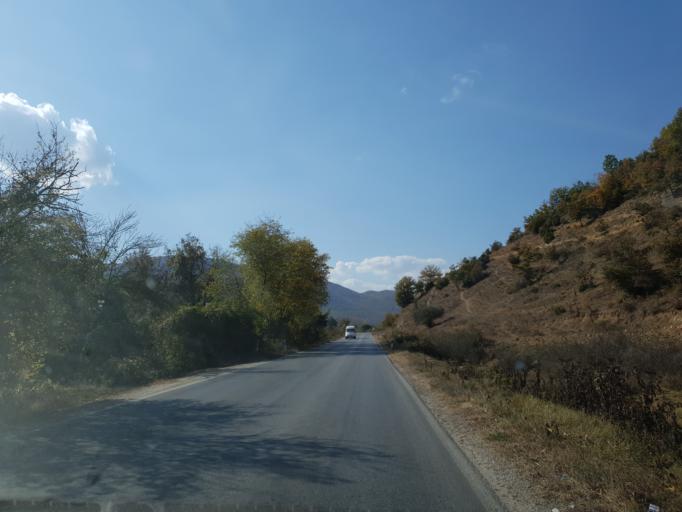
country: MK
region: Vranestica
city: Vranestica
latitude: 41.4692
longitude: 21.0232
